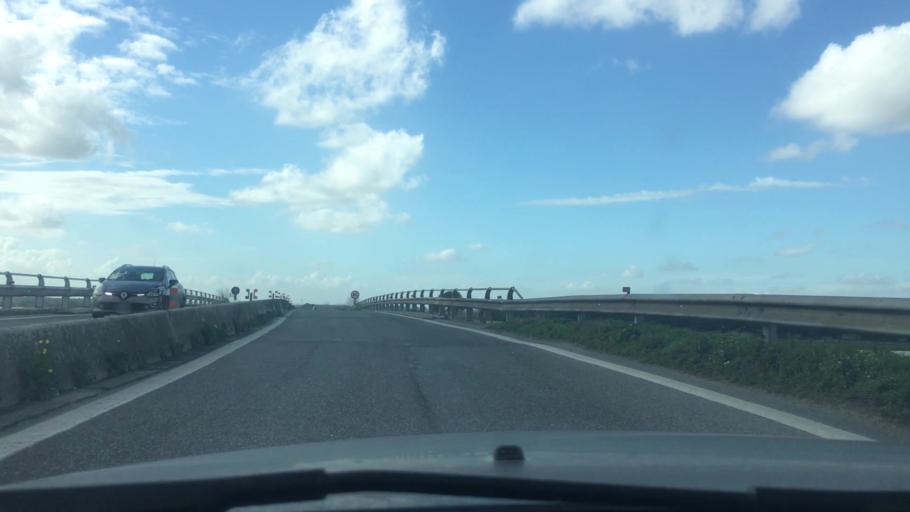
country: IT
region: Campania
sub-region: Provincia di Caserta
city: San Marco Evangelista
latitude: 41.0199
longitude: 14.3228
